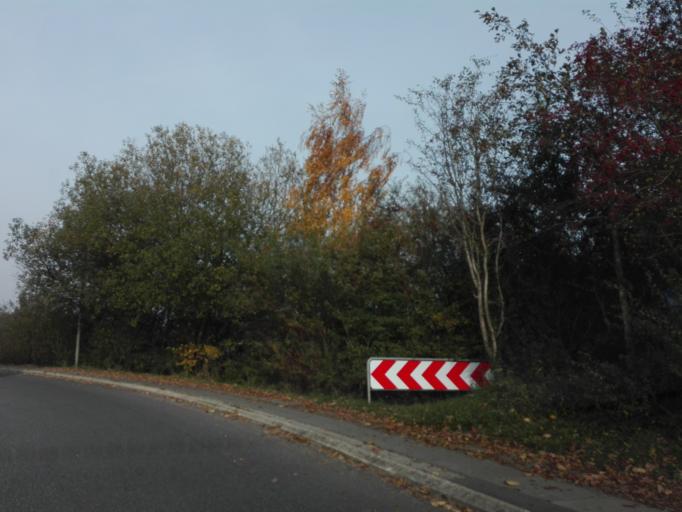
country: DK
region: Central Jutland
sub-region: Arhus Kommune
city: Solbjerg
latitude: 56.0457
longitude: 10.0826
